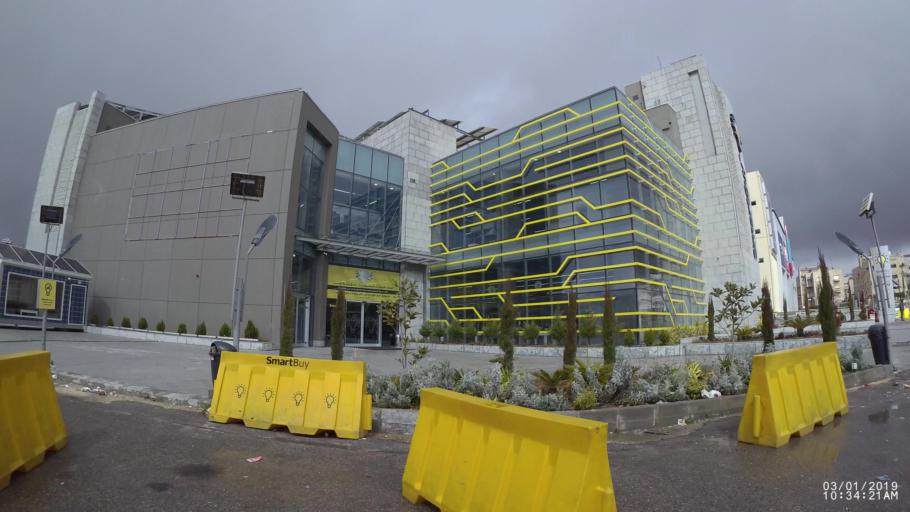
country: JO
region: Amman
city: Wadi as Sir
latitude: 31.9517
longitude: 35.8558
